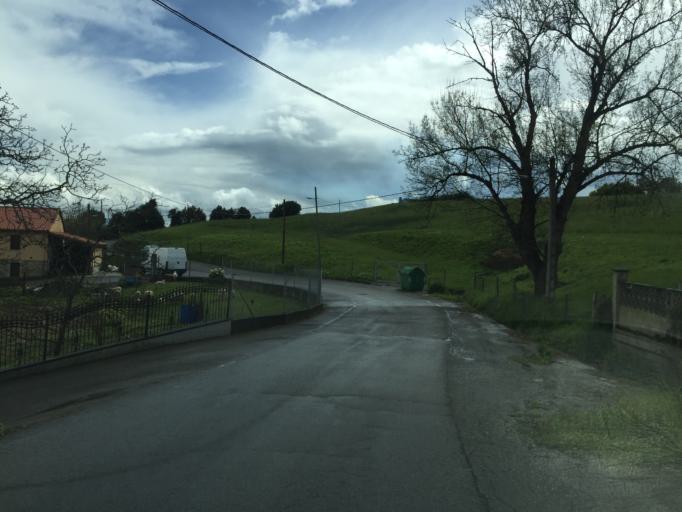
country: ES
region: Asturias
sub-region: Province of Asturias
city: Natahoyo
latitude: 43.5543
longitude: -5.7080
